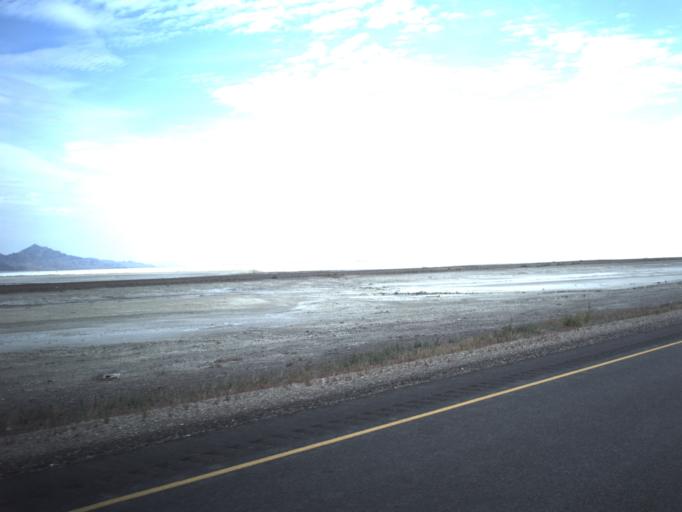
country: US
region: Utah
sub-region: Tooele County
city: Wendover
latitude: 40.7402
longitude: -113.9385
